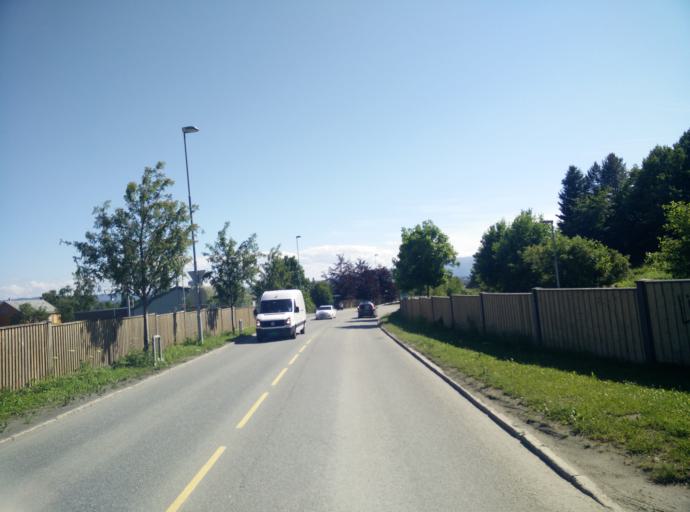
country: NO
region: Sor-Trondelag
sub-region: Trondheim
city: Trondheim
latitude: 63.4001
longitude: 10.3579
